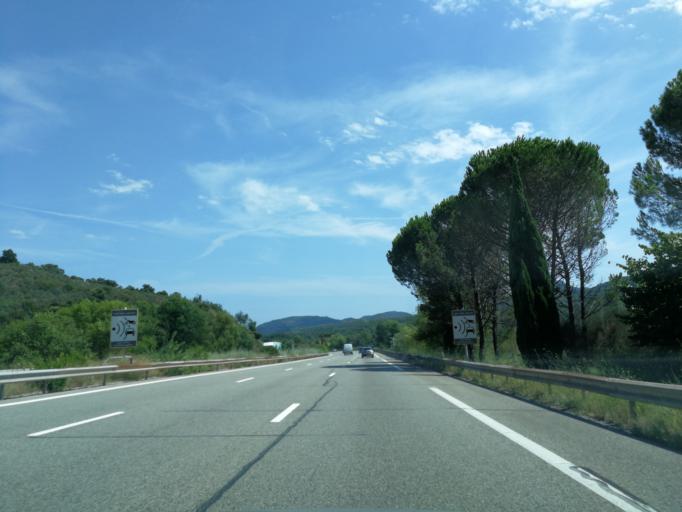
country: FR
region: Provence-Alpes-Cote d'Azur
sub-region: Departement du Var
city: Tanneron
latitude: 43.5374
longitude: 6.8594
